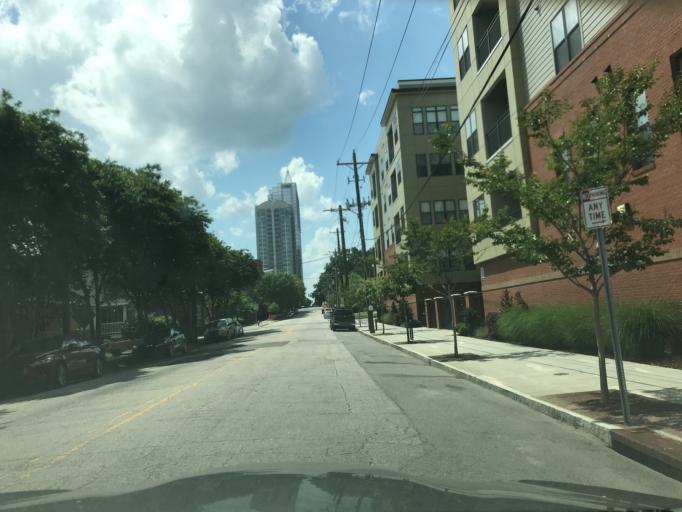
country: US
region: North Carolina
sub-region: Wake County
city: Raleigh
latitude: 35.7767
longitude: -78.6325
